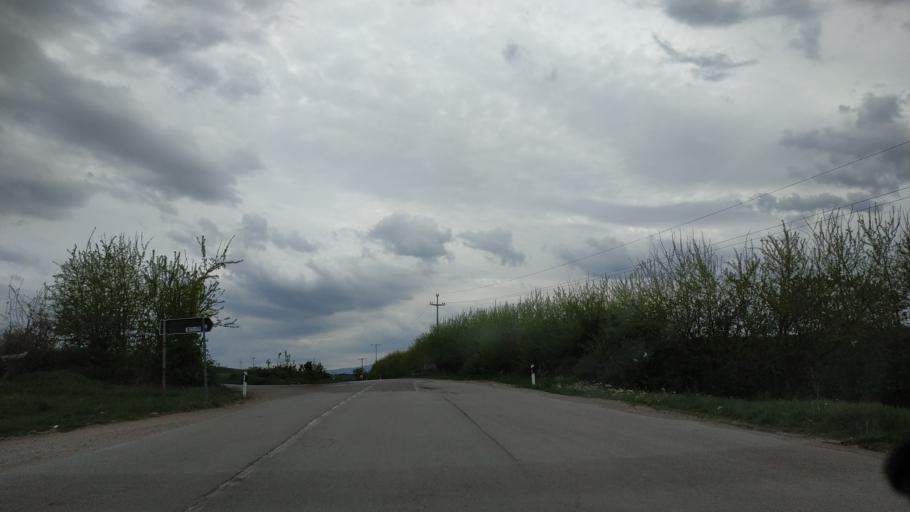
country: RS
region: Central Serbia
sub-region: Nisavski Okrug
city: Aleksinac
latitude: 43.6086
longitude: 21.6880
